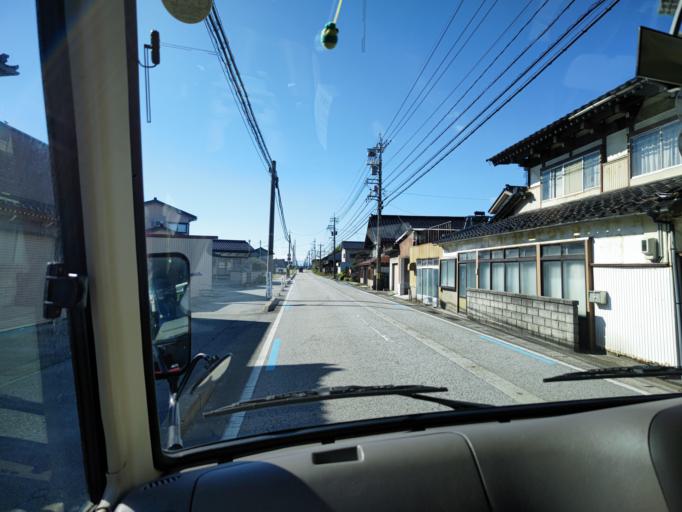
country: JP
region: Toyama
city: Nyuzen
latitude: 36.9043
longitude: 137.4245
